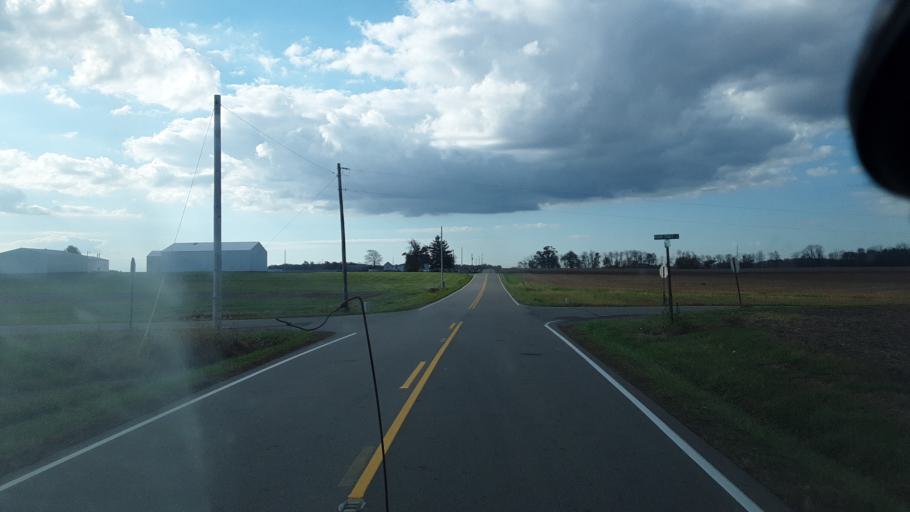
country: US
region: Ohio
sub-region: Fayette County
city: Washington Court House
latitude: 39.4411
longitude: -83.4384
